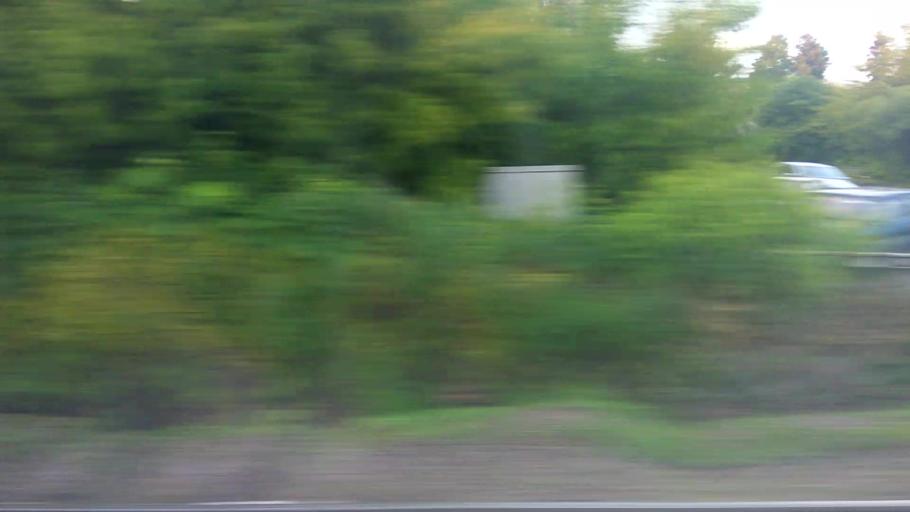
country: RU
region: Moskovskaya
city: Barybino
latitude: 55.2741
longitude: 37.8944
